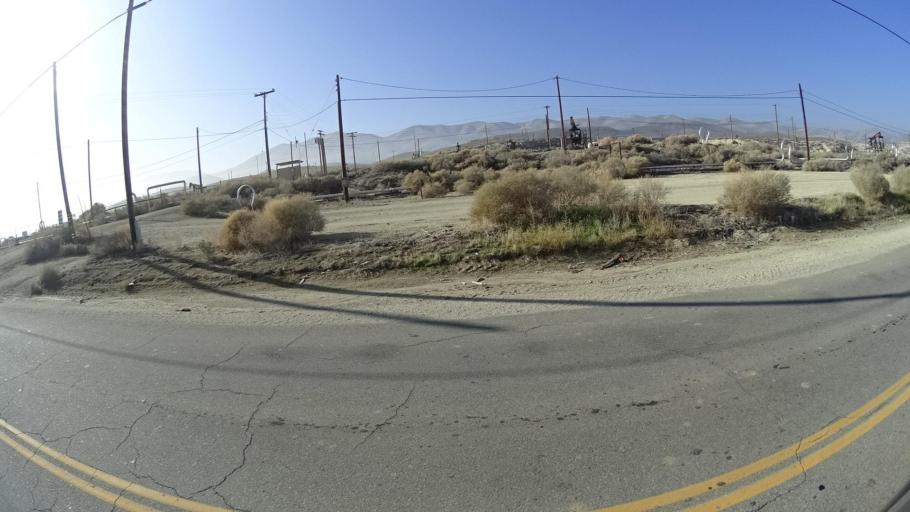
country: US
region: California
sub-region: Kern County
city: Taft Heights
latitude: 35.2033
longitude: -119.5950
